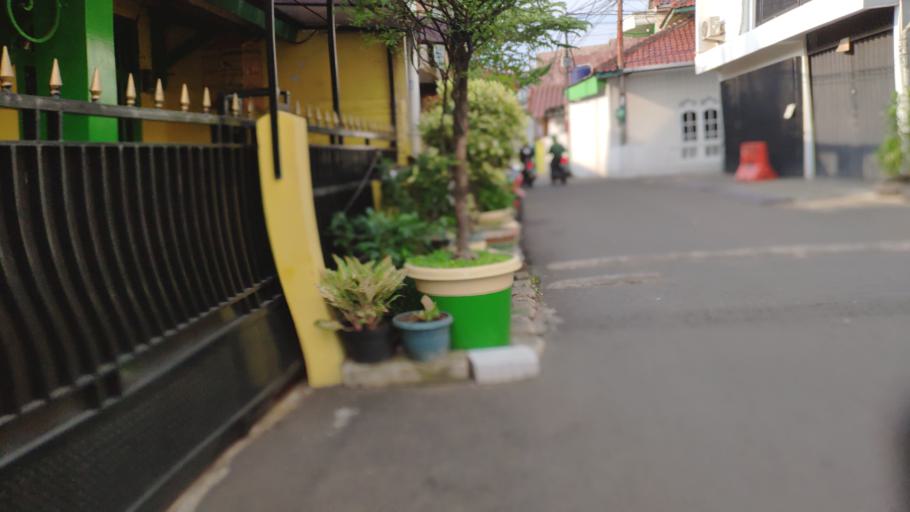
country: ID
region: West Java
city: Pamulang
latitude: -6.3054
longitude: 106.8064
